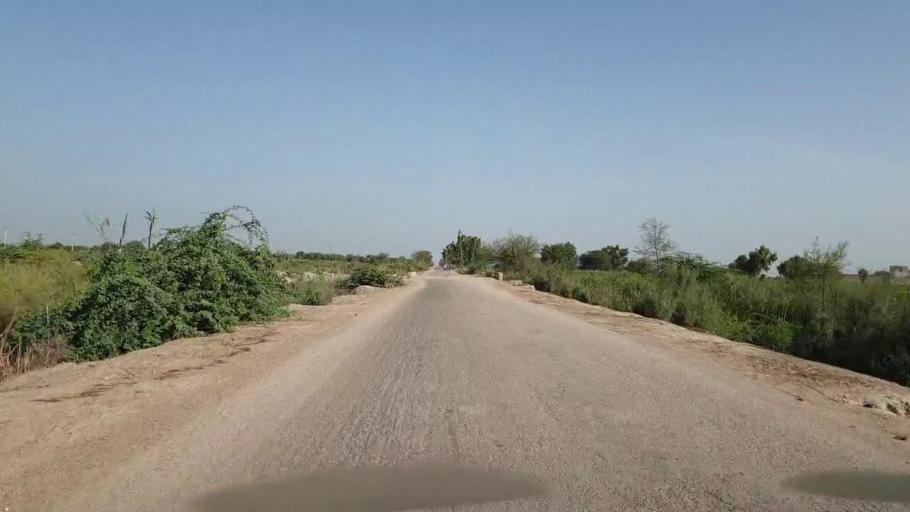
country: PK
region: Sindh
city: Nawabshah
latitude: 26.1648
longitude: 68.4423
